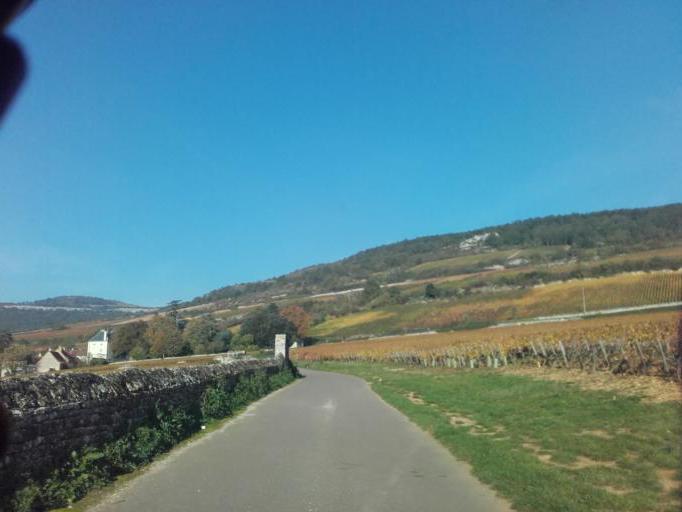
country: FR
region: Bourgogne
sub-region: Departement de Saone-et-Loire
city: Chagny
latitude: 46.9149
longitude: 4.6997
